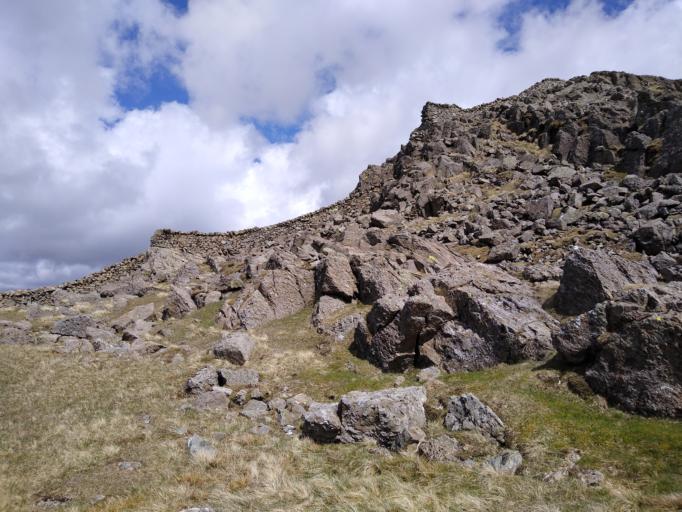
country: GB
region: England
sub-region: Cumbria
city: Frizington
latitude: 54.4868
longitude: -3.3294
